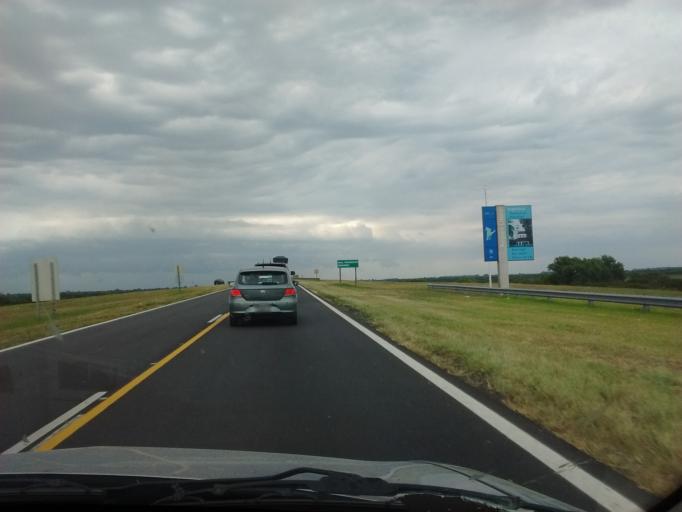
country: AR
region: Santa Fe
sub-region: Departamento de Rosario
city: Rosario
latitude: -32.8629
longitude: -60.6328
